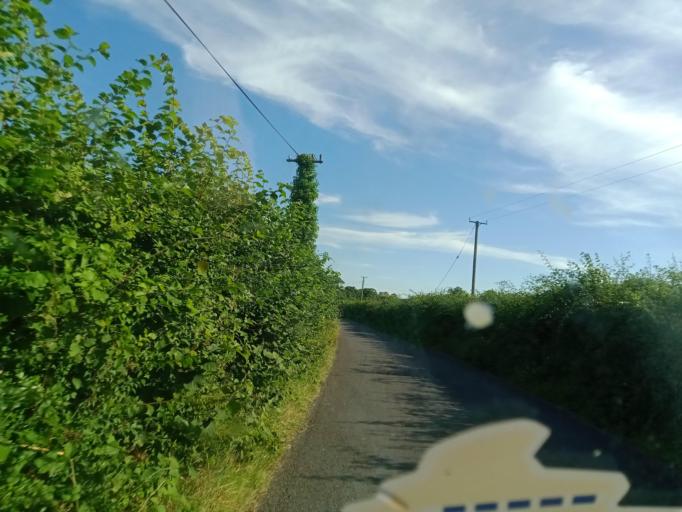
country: IE
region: Leinster
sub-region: Kilkenny
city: Ballyragget
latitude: 52.7586
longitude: -7.3913
